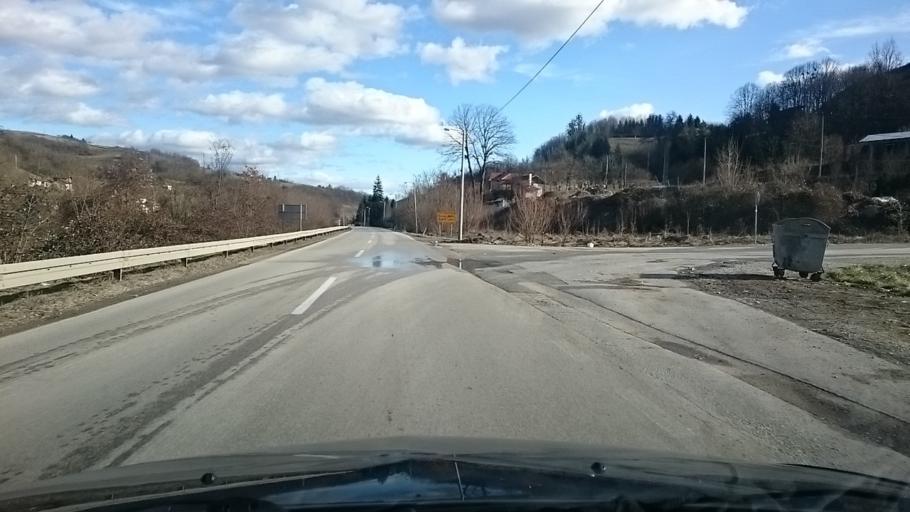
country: BA
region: Republika Srpska
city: Hiseti
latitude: 44.7081
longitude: 17.1711
